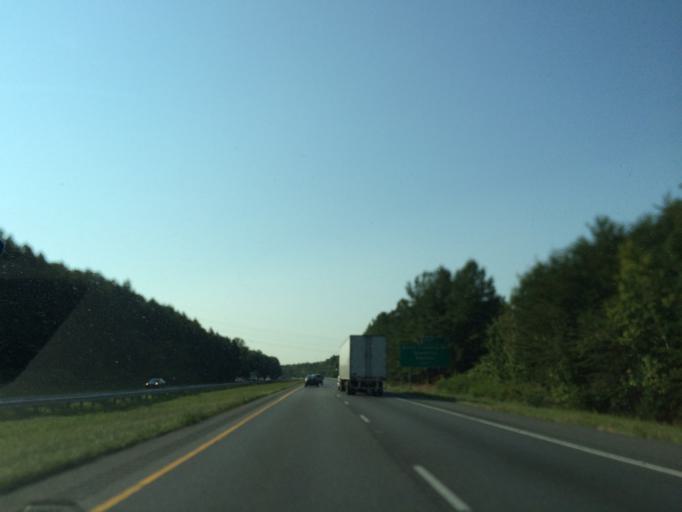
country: US
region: Maryland
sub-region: Anne Arundel County
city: Odenton
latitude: 39.0895
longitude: -76.6863
